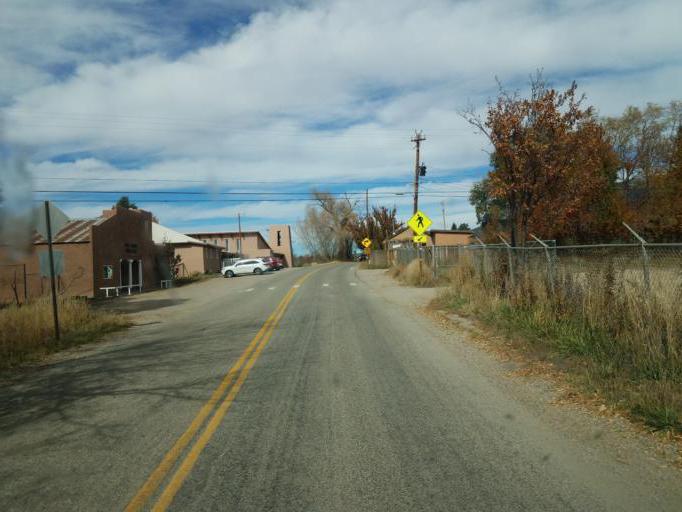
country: US
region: New Mexico
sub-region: Taos County
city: Arroyo Seco
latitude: 36.5169
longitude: -105.5689
